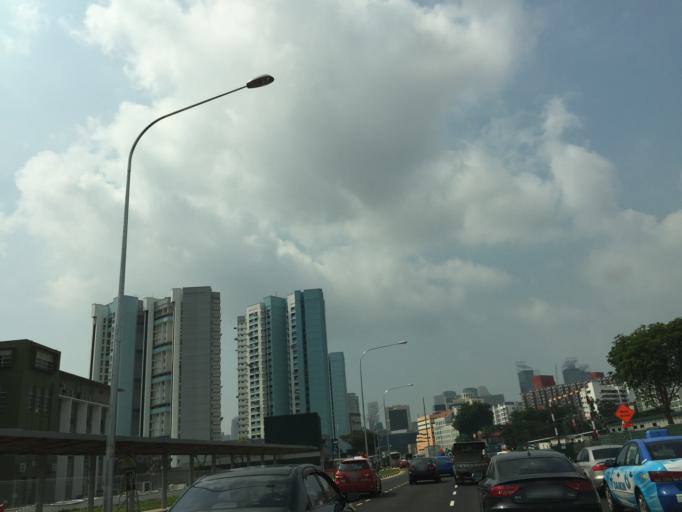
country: SG
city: Singapore
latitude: 1.3075
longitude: 103.8482
